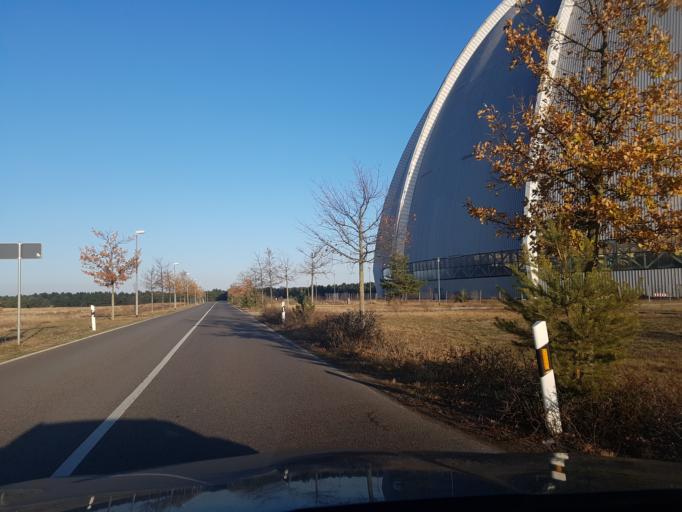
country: DE
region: Brandenburg
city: Halbe
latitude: 52.0374
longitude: 13.7458
